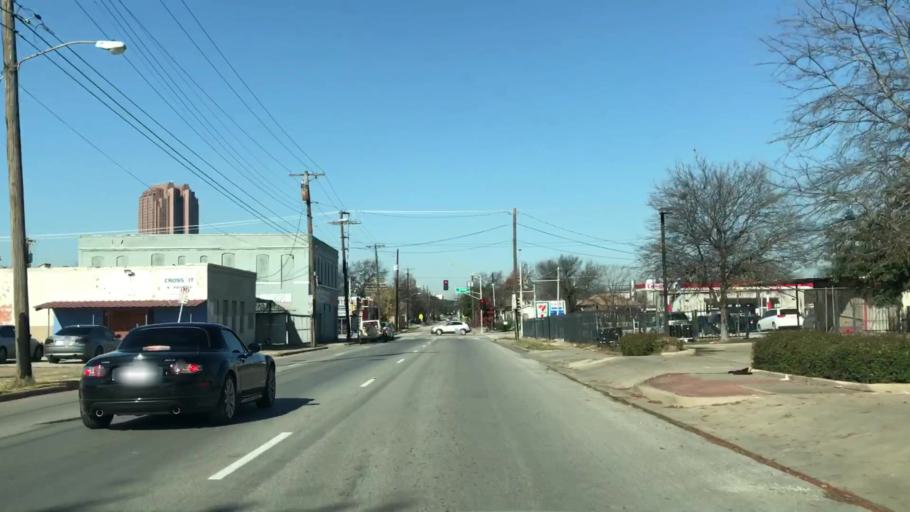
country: US
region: Texas
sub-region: Dallas County
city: Dallas
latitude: 32.8007
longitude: -96.7814
